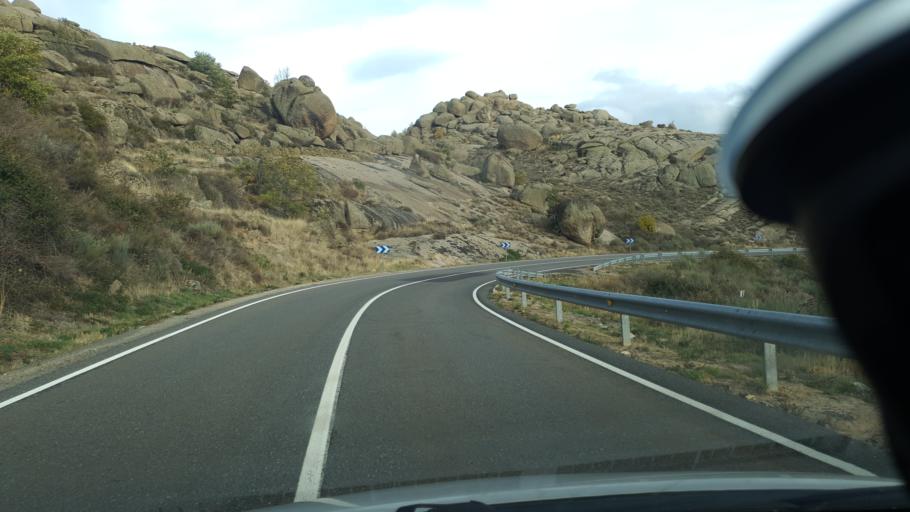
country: ES
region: Castille and Leon
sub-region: Provincia de Avila
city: Navalosa
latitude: 40.3959
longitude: -4.9175
